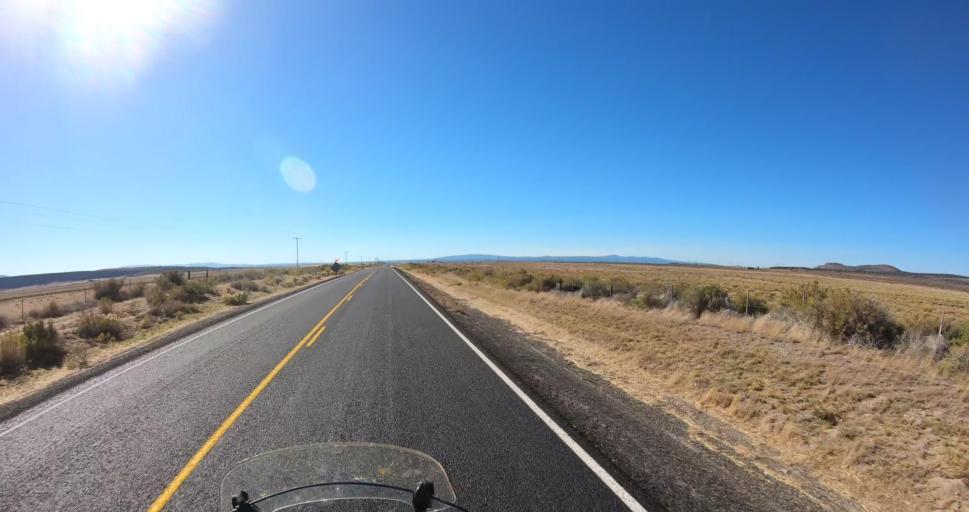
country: US
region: Oregon
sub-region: Deschutes County
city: La Pine
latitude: 43.1309
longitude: -120.9106
